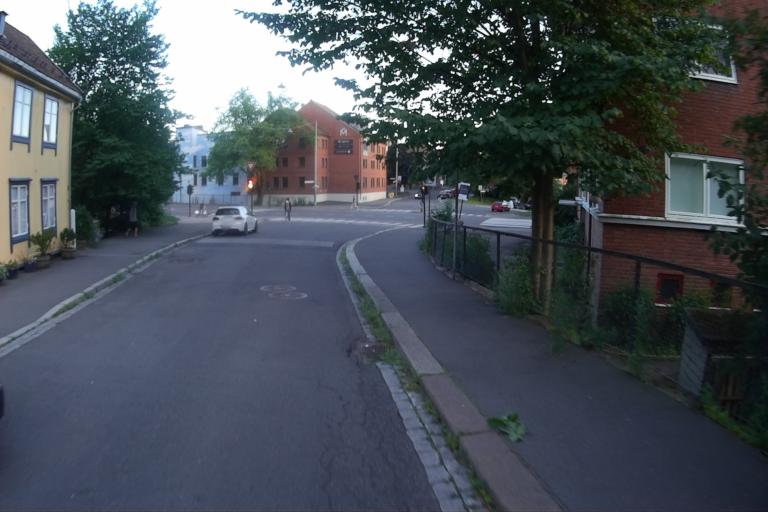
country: NO
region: Oslo
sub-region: Oslo
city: Oslo
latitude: 59.9340
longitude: 10.7562
